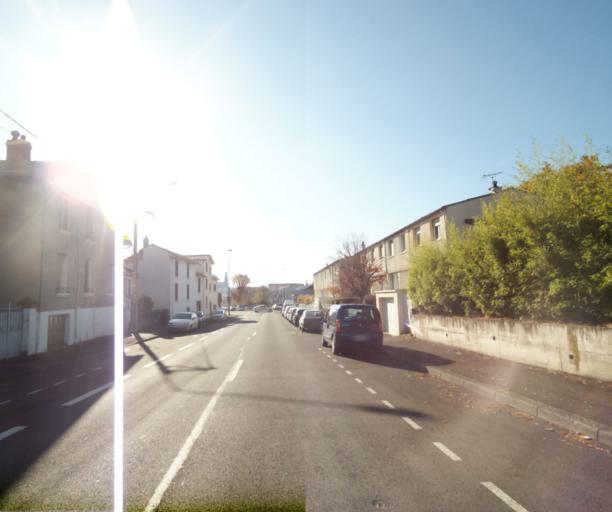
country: FR
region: Auvergne
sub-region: Departement du Puy-de-Dome
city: Clermont-Ferrand
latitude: 45.7913
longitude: 3.0840
